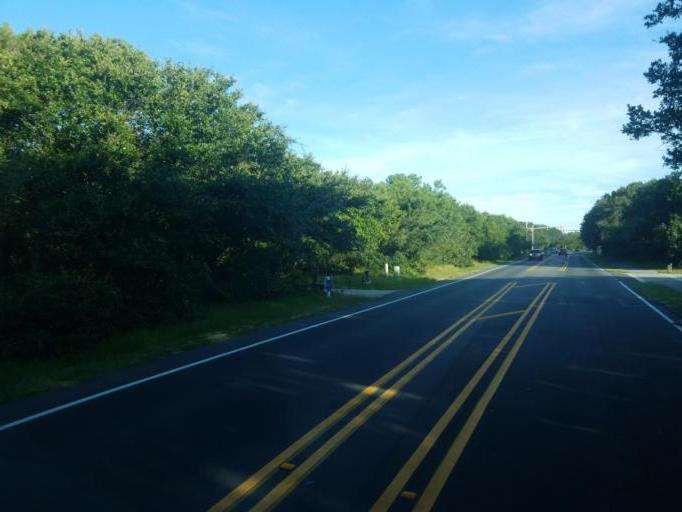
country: US
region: North Carolina
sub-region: Dare County
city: Southern Shores
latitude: 36.1430
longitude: -75.7389
